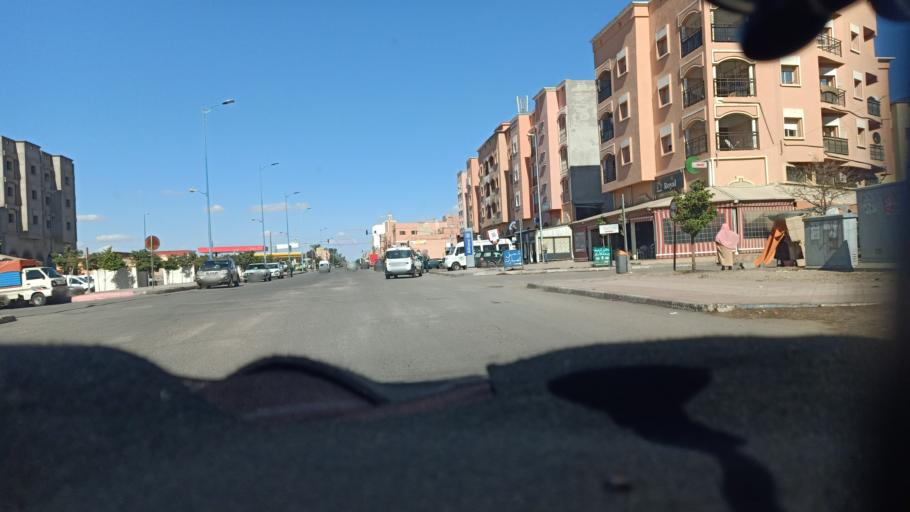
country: MA
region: Doukkala-Abda
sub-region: Safi
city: Youssoufia
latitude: 32.2406
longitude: -8.5386
